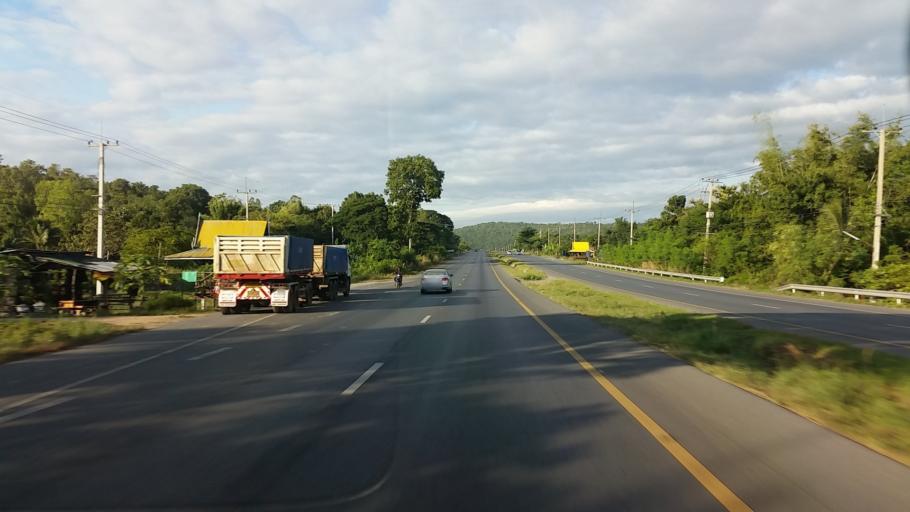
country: TH
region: Lop Buri
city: Phatthana Nikhom
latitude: 14.9831
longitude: 100.9181
